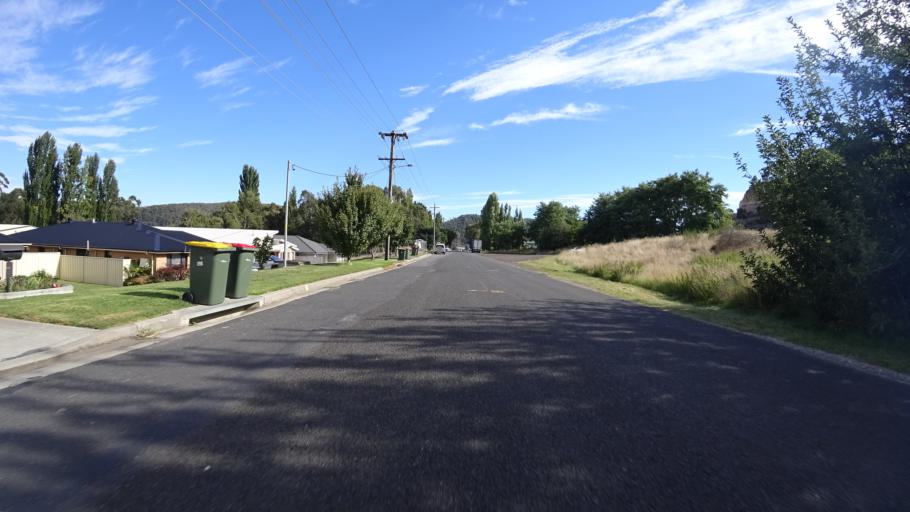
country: AU
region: New South Wales
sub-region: Lithgow
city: Lithgow
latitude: -33.4796
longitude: 150.1750
